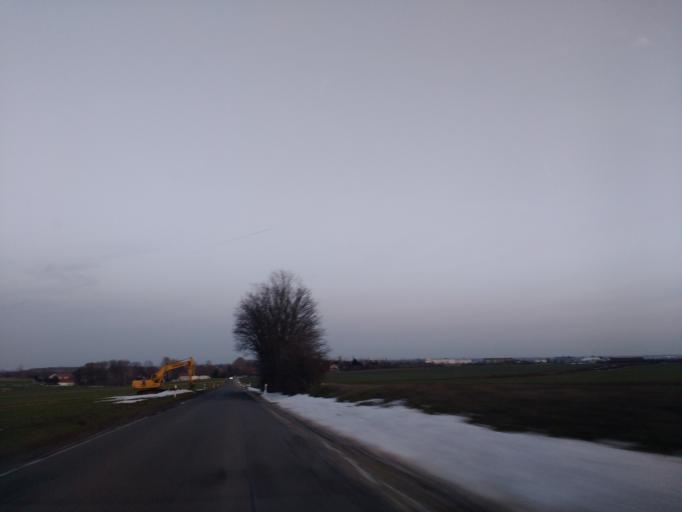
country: DE
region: Saxony-Anhalt
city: Oppin
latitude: 51.5550
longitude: 12.0097
